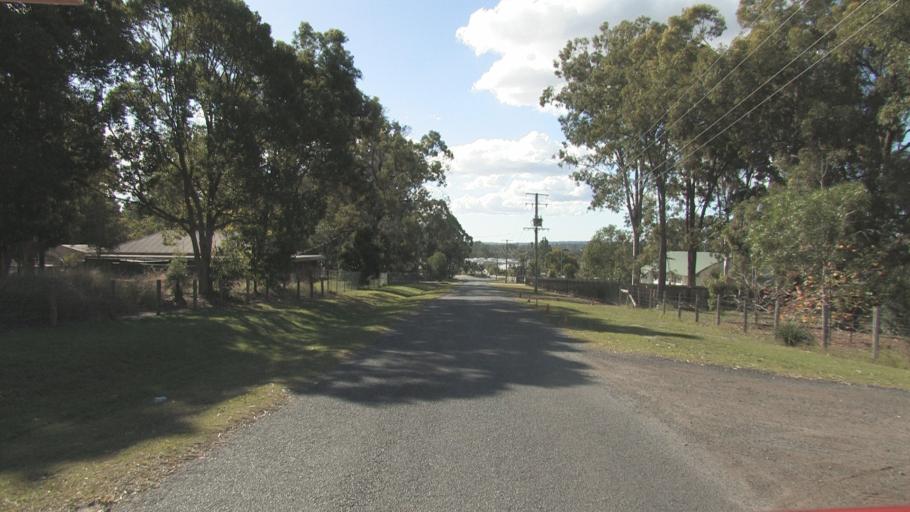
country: AU
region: Queensland
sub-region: Logan
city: Logan Reserve
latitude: -27.7154
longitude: 153.1111
